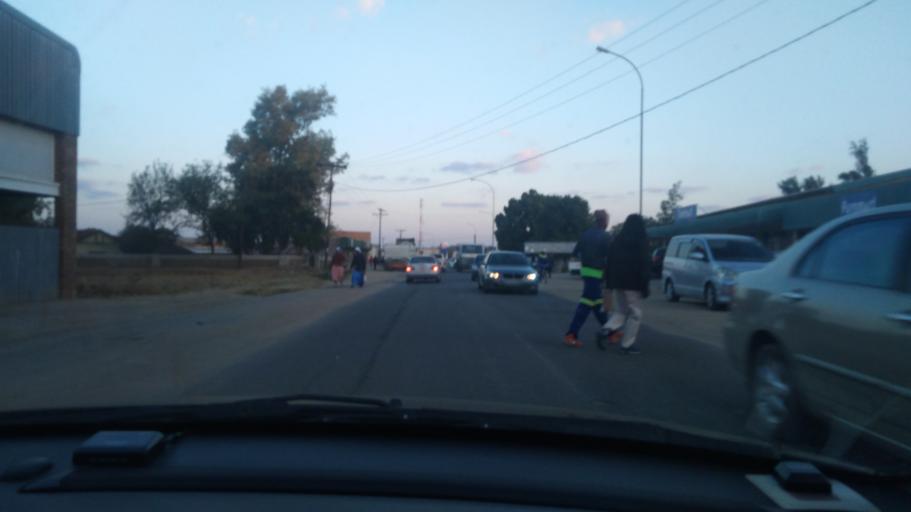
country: BW
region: Central
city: Mahalapye
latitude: -23.1067
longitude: 26.8324
